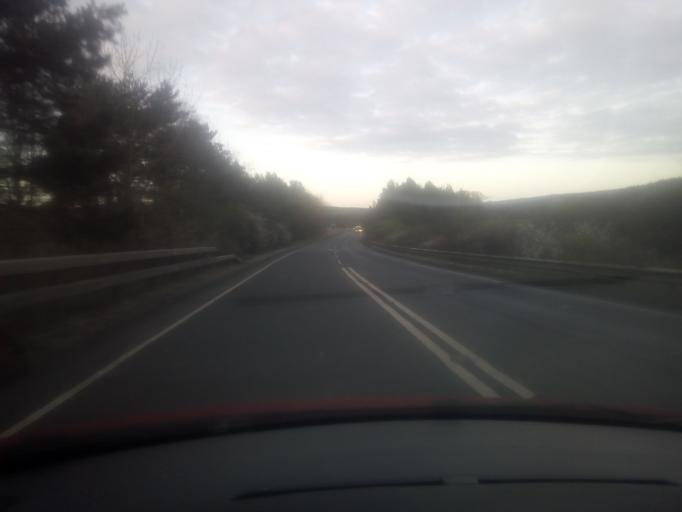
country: GB
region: England
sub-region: Northumberland
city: Healey
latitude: 54.9468
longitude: -1.9630
